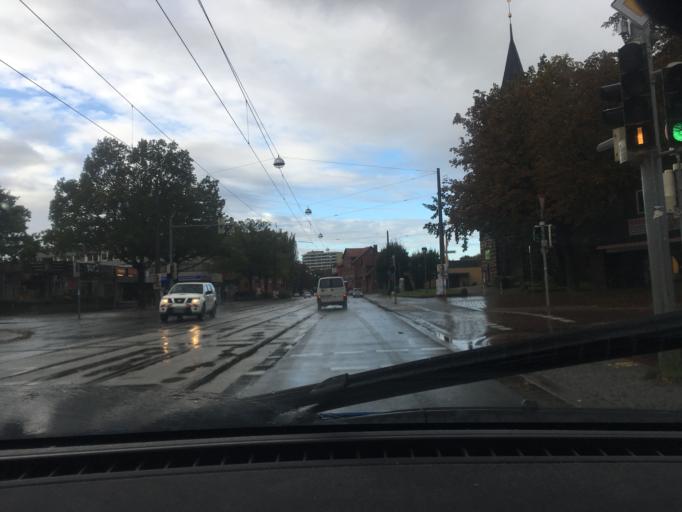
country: DE
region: Lower Saxony
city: Langenhagen
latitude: 52.4124
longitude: 9.7985
